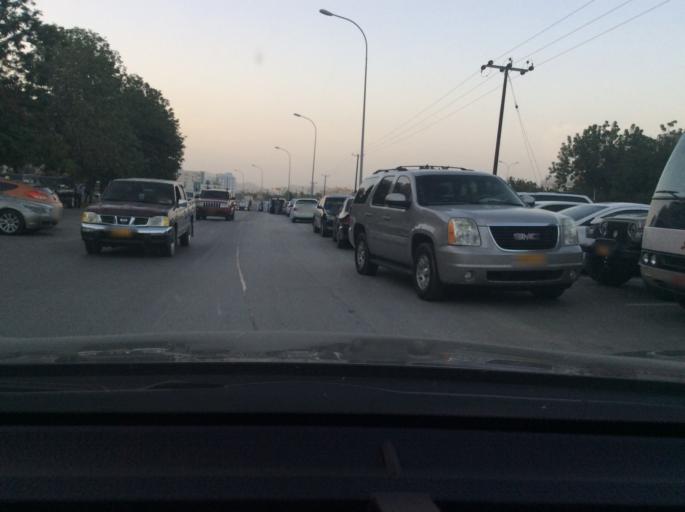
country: OM
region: Muhafazat Masqat
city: Muscat
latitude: 23.5763
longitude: 58.5645
